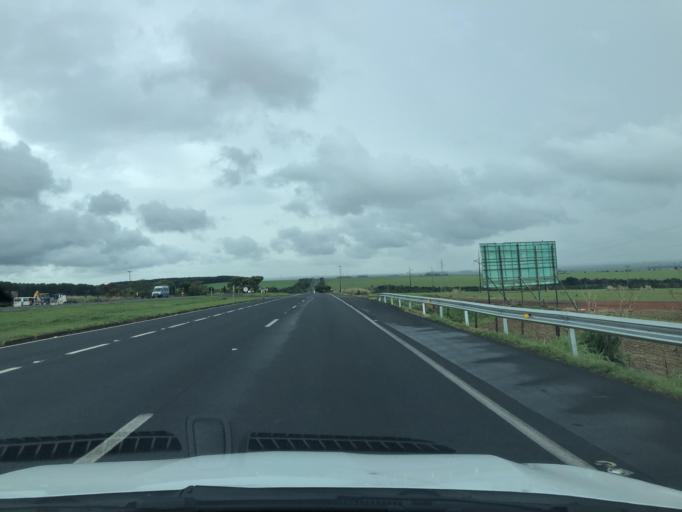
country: BR
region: Minas Gerais
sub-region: Uberlandia
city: Uberlandia
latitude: -19.0773
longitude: -48.1887
